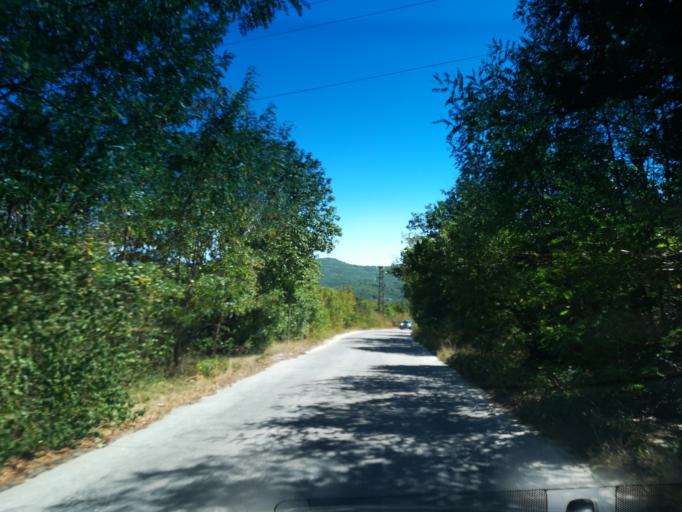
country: BG
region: Pazardzhik
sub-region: Obshtina Strelcha
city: Strelcha
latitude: 42.5424
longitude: 24.3312
